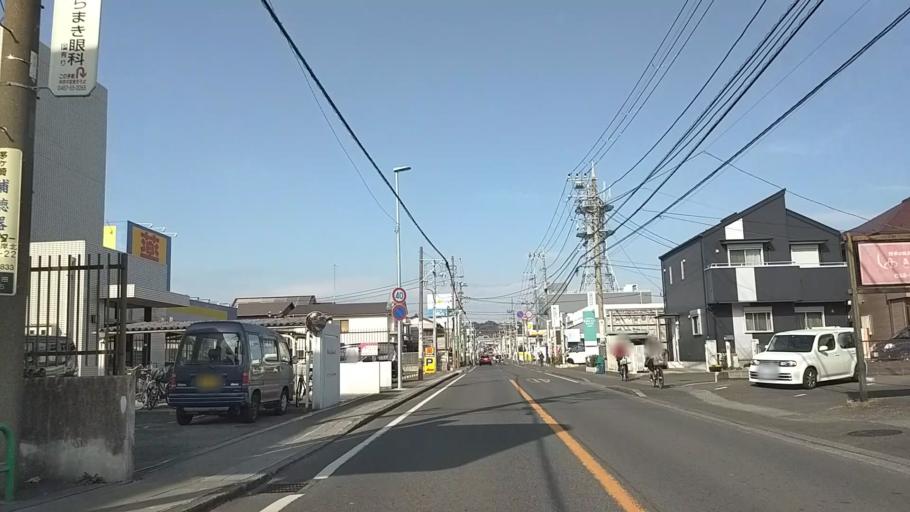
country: JP
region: Kanagawa
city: Chigasaki
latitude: 35.3446
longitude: 139.4125
